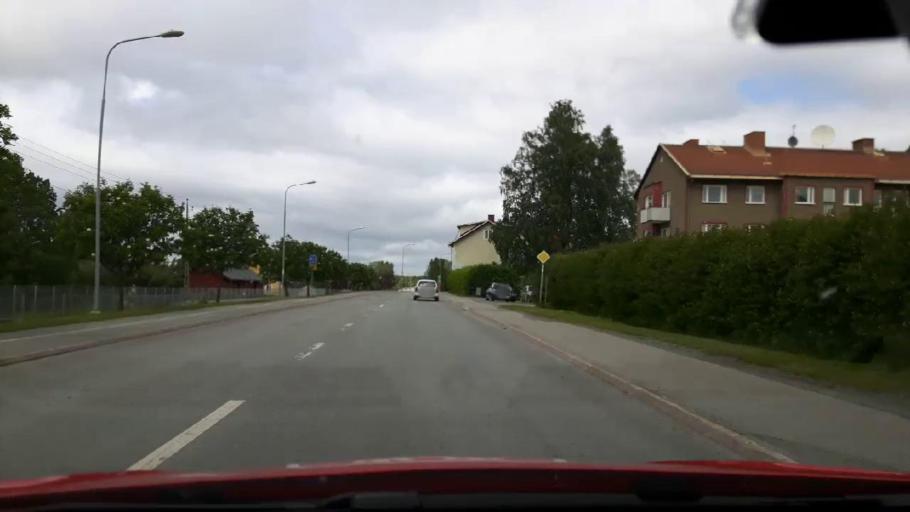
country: SE
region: Jaemtland
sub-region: Krokoms Kommun
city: Krokom
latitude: 63.3249
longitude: 14.4500
